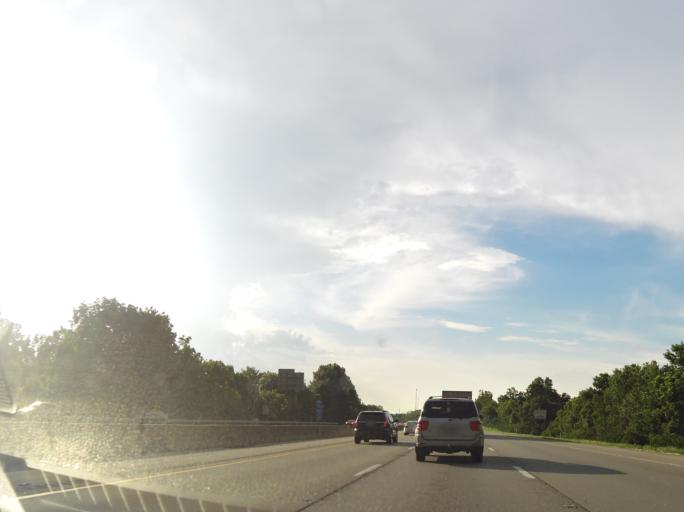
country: US
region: Kentucky
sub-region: Fayette County
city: Lexington-Fayette
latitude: 38.0818
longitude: -84.4601
